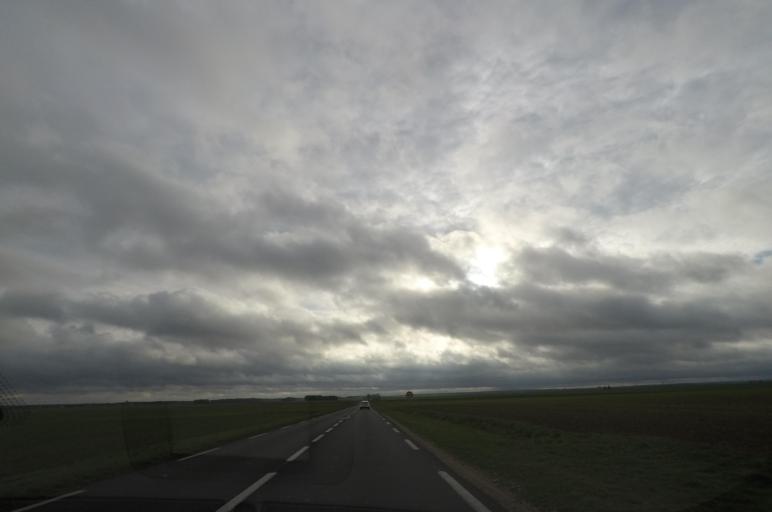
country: FR
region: Centre
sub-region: Departement du Loir-et-Cher
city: Herbault
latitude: 47.7092
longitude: 1.1670
